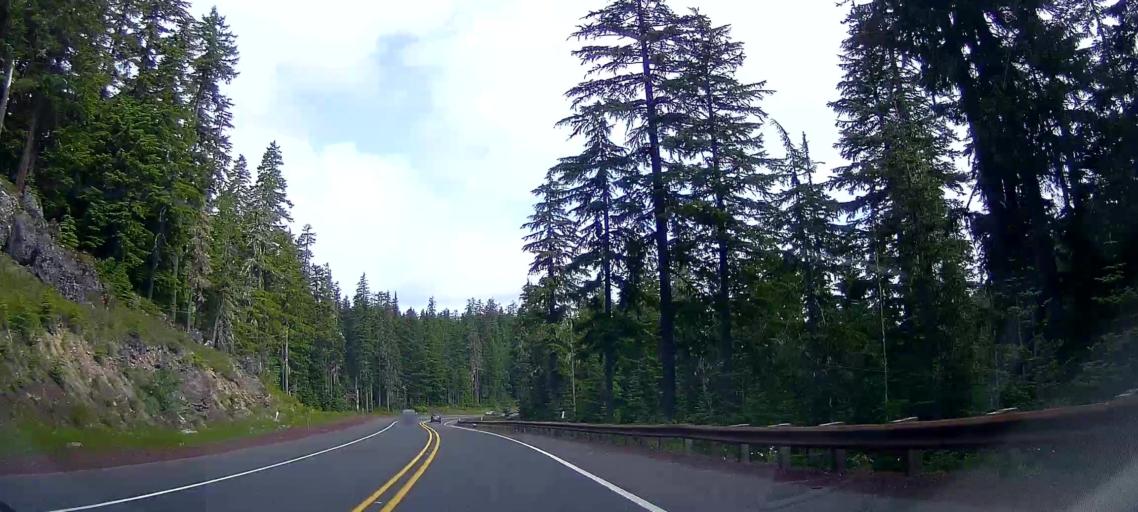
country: US
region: Oregon
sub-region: Clackamas County
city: Mount Hood Village
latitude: 45.2189
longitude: -121.6981
